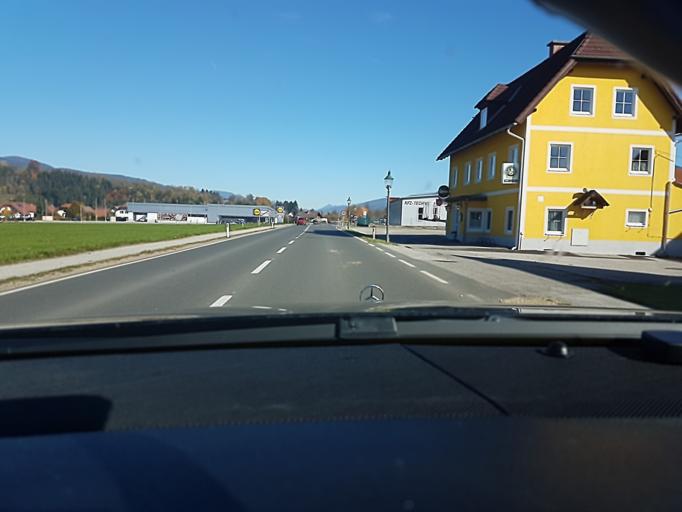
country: AT
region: Styria
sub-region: Politischer Bezirk Bruck-Muerzzuschlag
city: Krieglach
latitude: 47.5431
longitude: 15.5411
